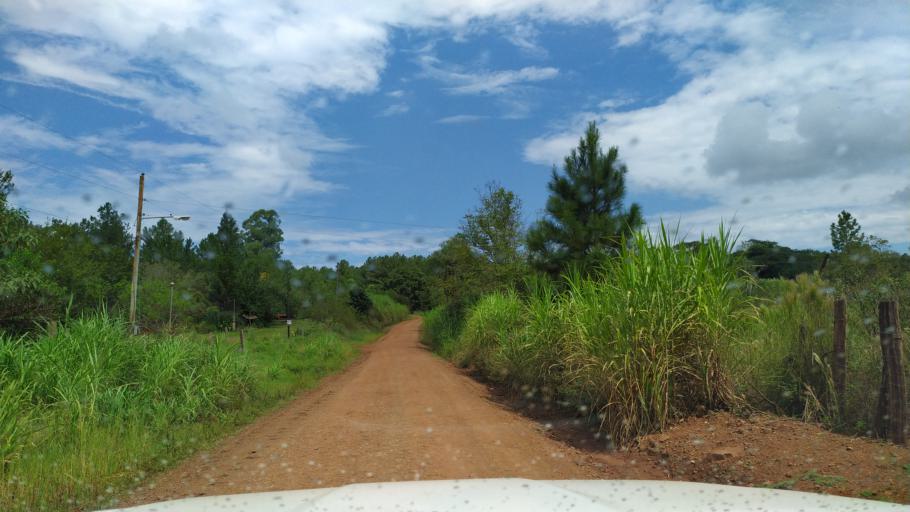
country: AR
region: Misiones
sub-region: Departamento de Eldorado
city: Eldorado
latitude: -26.4927
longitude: -54.5863
